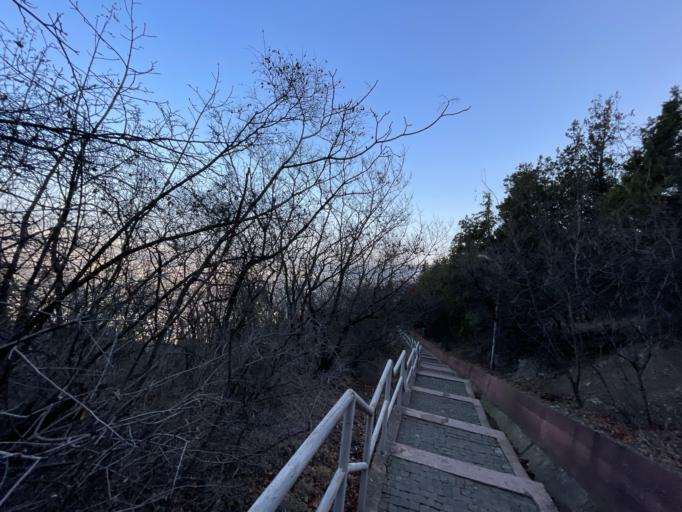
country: GE
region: T'bilisi
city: Tbilisi
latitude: 41.6935
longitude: 44.7879
